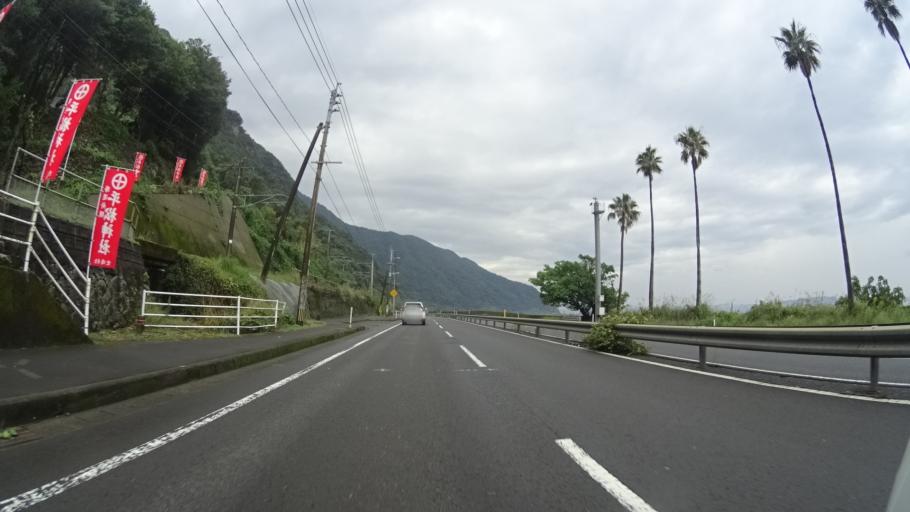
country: JP
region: Kagoshima
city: Kajiki
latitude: 31.6709
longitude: 130.6119
